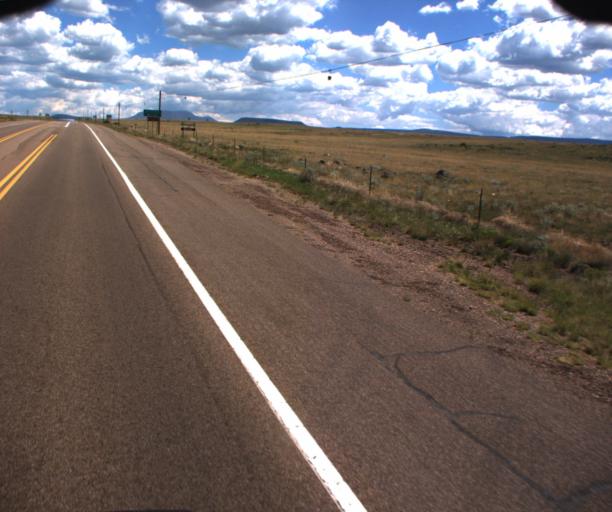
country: US
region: Arizona
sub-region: Apache County
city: Springerville
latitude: 34.1753
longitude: -109.3200
